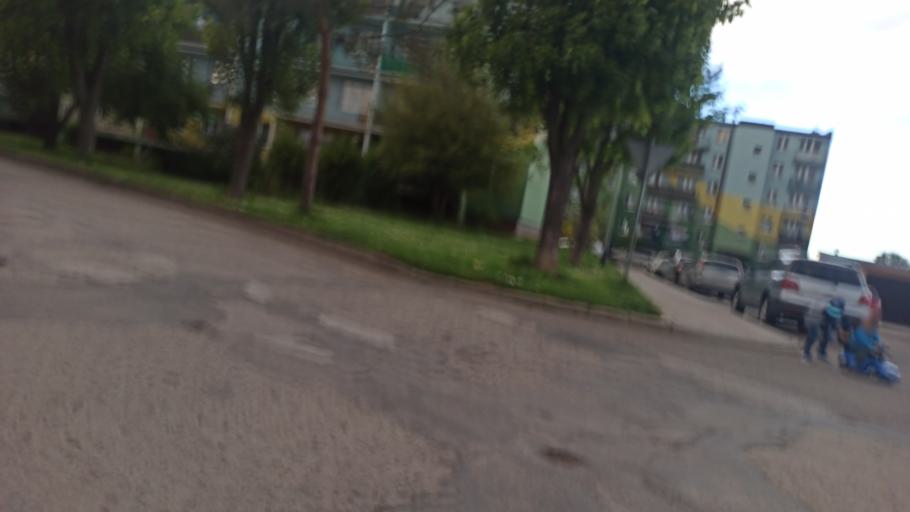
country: PL
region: Subcarpathian Voivodeship
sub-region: Powiat jaroslawski
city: Radymno
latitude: 49.9456
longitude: 22.8295
